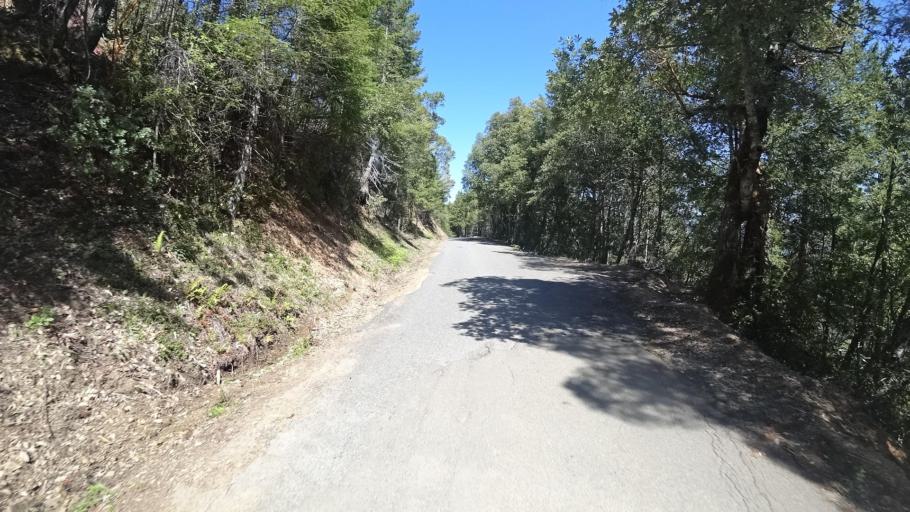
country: US
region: California
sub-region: Humboldt County
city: Redway
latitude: 40.1517
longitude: -124.0648
